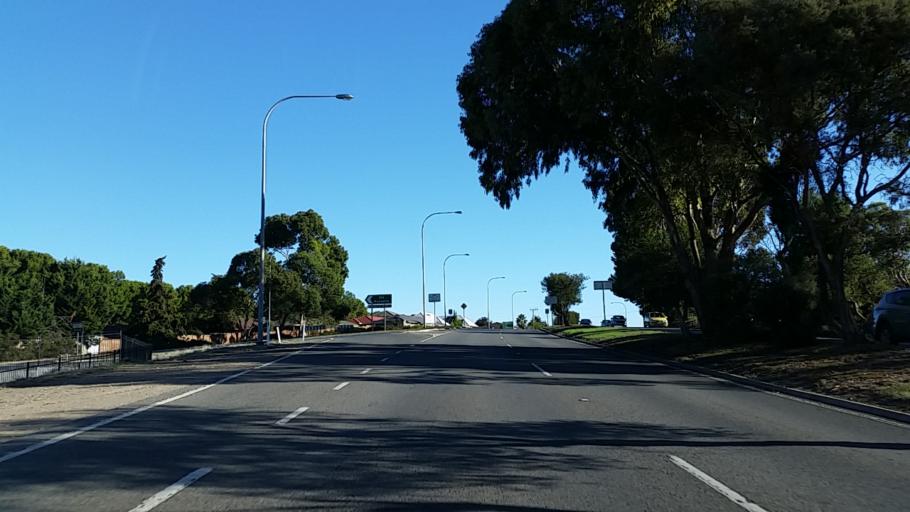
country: AU
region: South Australia
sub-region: Onkaparinga
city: Reynella
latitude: -35.0963
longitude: 138.5359
